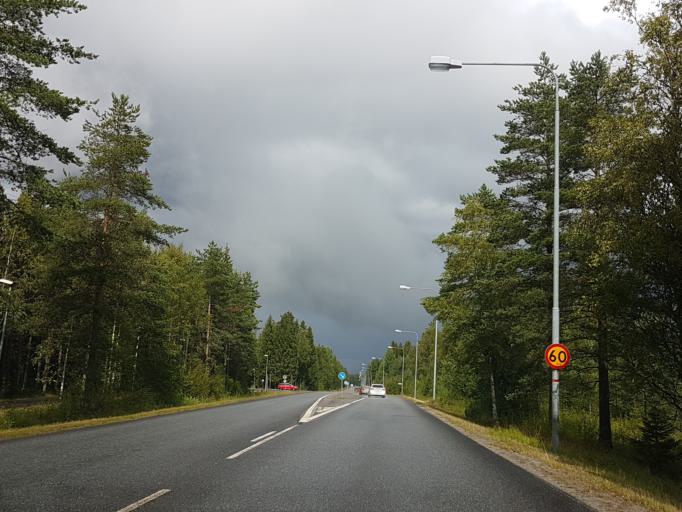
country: SE
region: Vaesterbotten
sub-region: Umea Kommun
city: Ersmark
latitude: 63.8513
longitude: 20.3436
